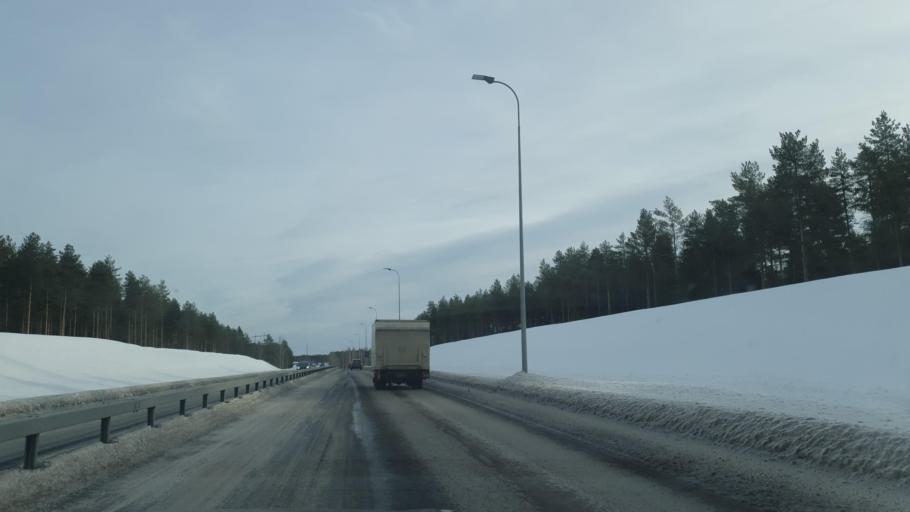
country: FI
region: Northern Ostrobothnia
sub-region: Oulu
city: Kempele
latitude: 64.9748
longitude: 25.5922
